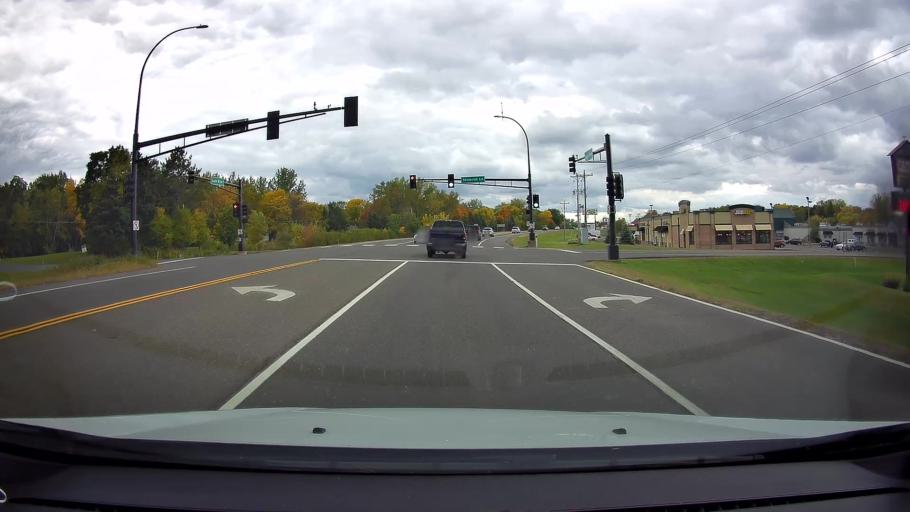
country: US
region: Minnesota
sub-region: Chisago County
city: Chisago City
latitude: 45.3803
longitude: -92.8716
